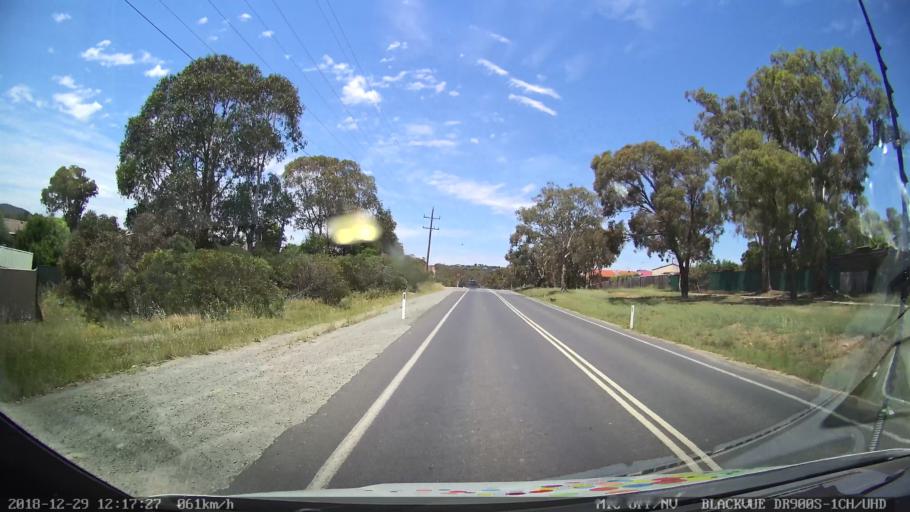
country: AU
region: New South Wales
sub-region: Queanbeyan
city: Queanbeyan
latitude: -35.3753
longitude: 149.2337
